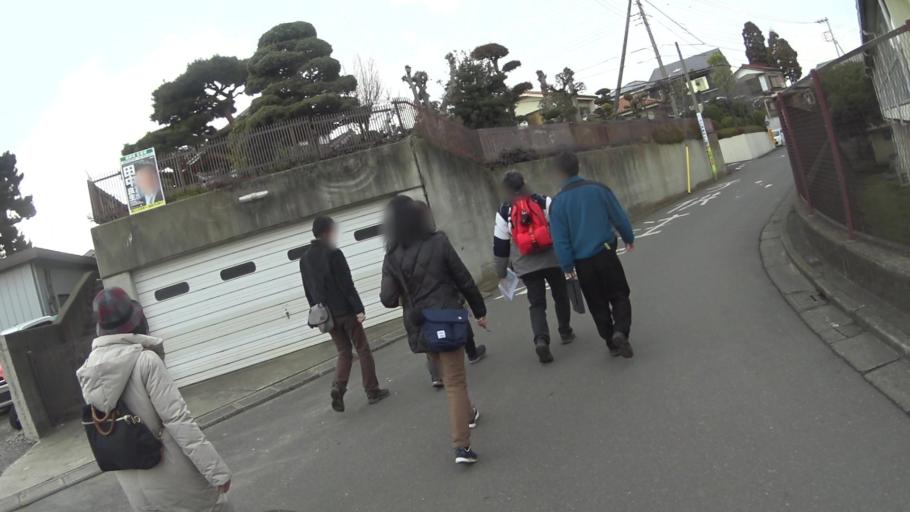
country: JP
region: Saitama
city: Shimotoda
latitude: 35.8533
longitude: 139.6848
